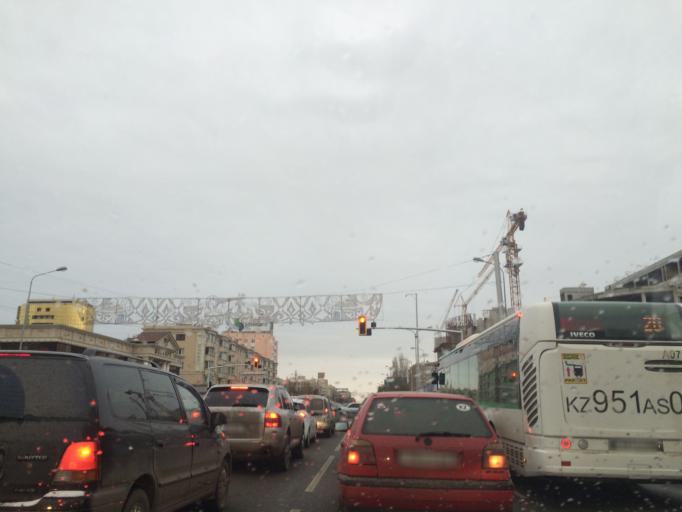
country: KZ
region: Astana Qalasy
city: Astana
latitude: 51.1623
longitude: 71.4285
